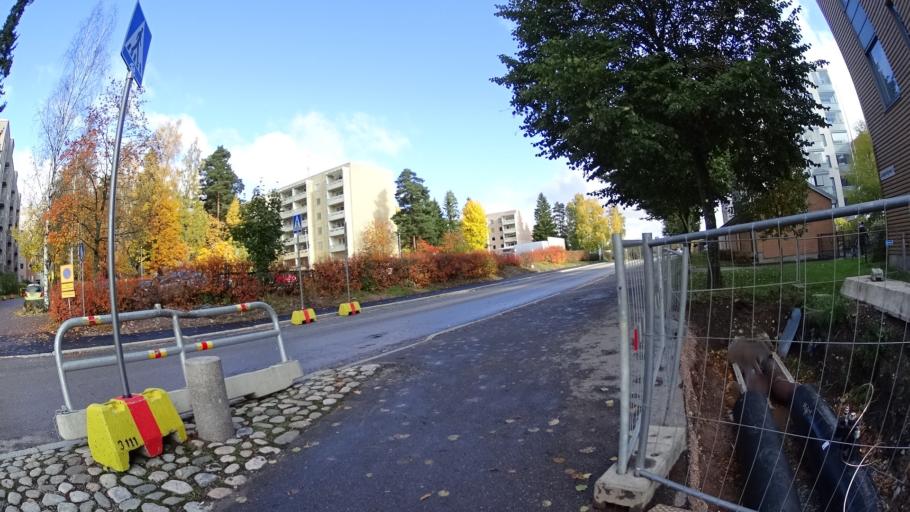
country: FI
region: Uusimaa
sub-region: Helsinki
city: Teekkarikylae
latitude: 60.2771
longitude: 24.8491
